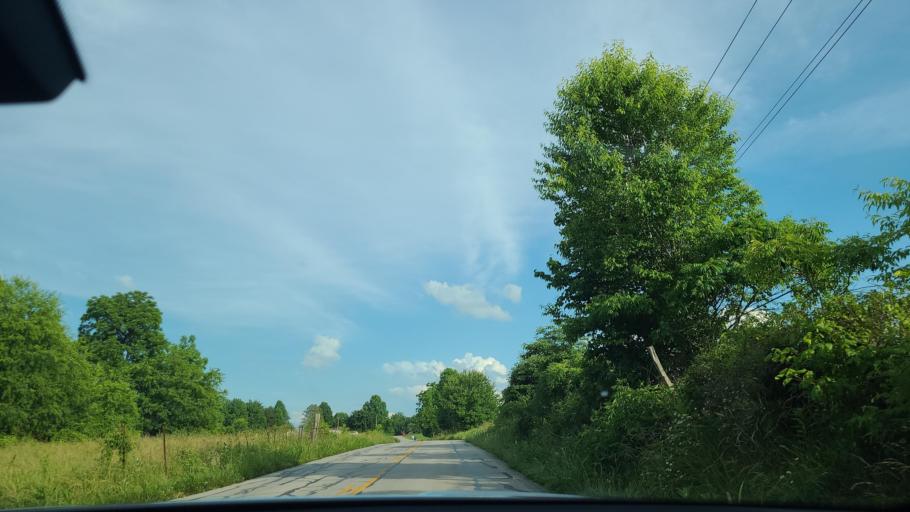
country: US
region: Kentucky
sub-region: Whitley County
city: Corbin
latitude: 36.8987
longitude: -84.2344
